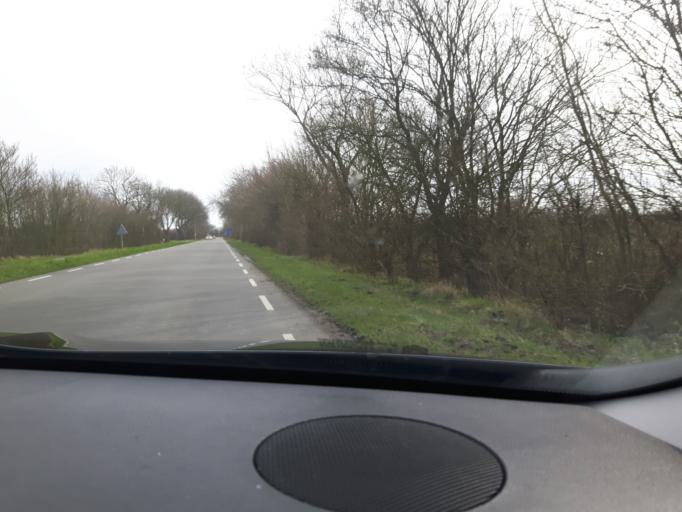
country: NL
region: Zeeland
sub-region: Gemeente Middelburg
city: Middelburg
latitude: 51.5118
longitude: 3.5997
